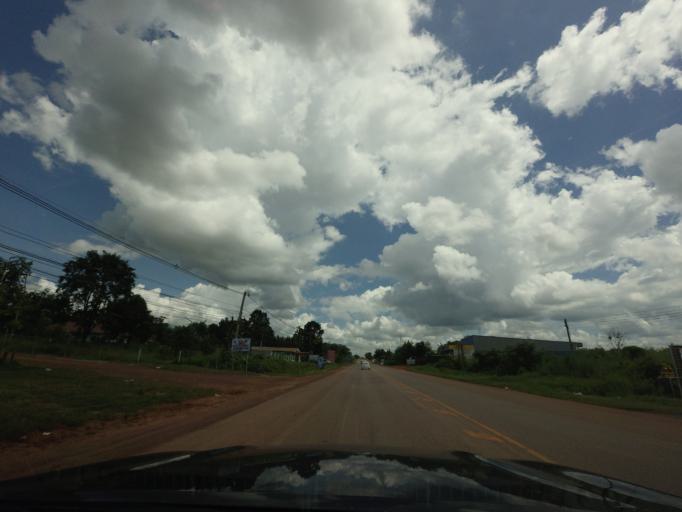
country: TH
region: Changwat Udon Thani
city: Ban Dung
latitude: 17.6778
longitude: 103.2450
